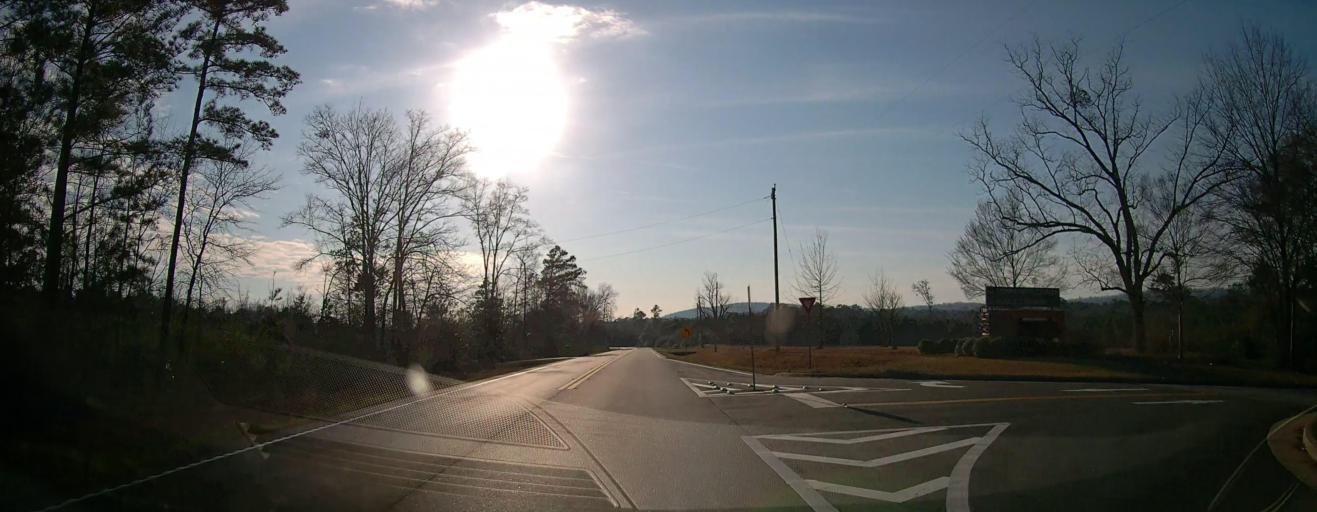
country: US
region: Georgia
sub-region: Harris County
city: Hamilton
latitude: 32.7529
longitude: -84.9012
